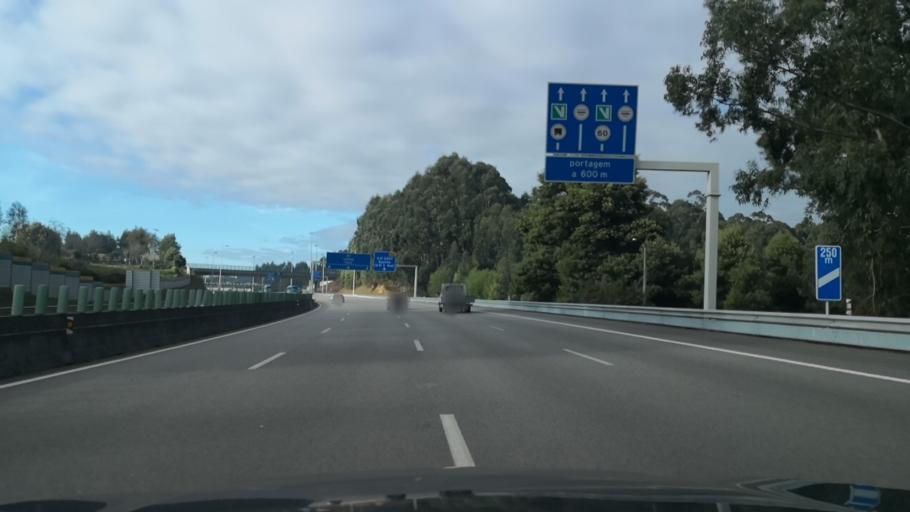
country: PT
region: Porto
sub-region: Vila Nova de Gaia
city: Grijo
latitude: 41.0220
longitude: -8.5789
